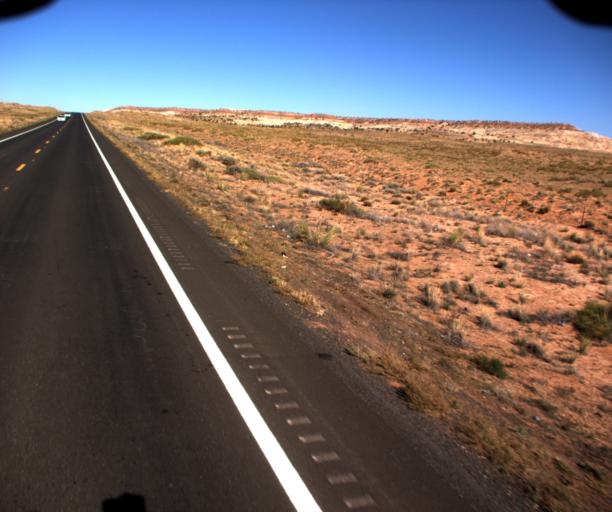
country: US
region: Arizona
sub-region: Coconino County
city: Tuba City
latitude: 36.2192
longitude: -111.0420
